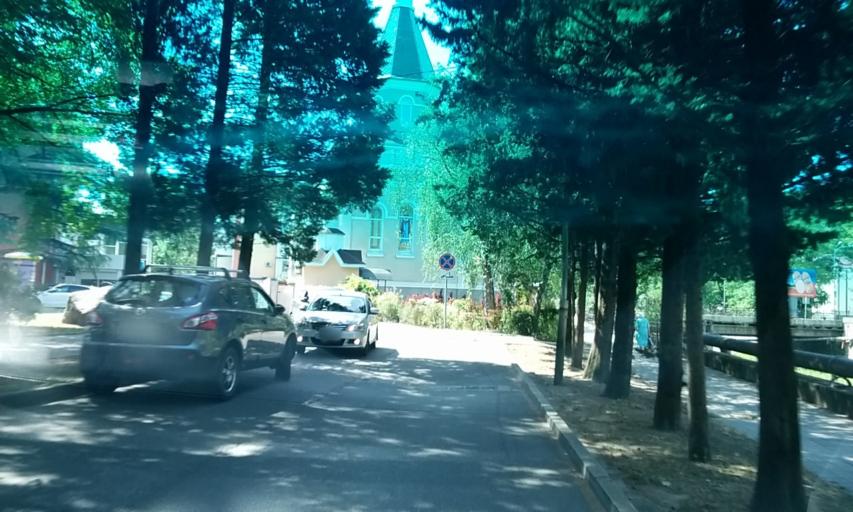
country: RU
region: Krasnodarskiy
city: Tuapse
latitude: 44.1068
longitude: 39.0597
